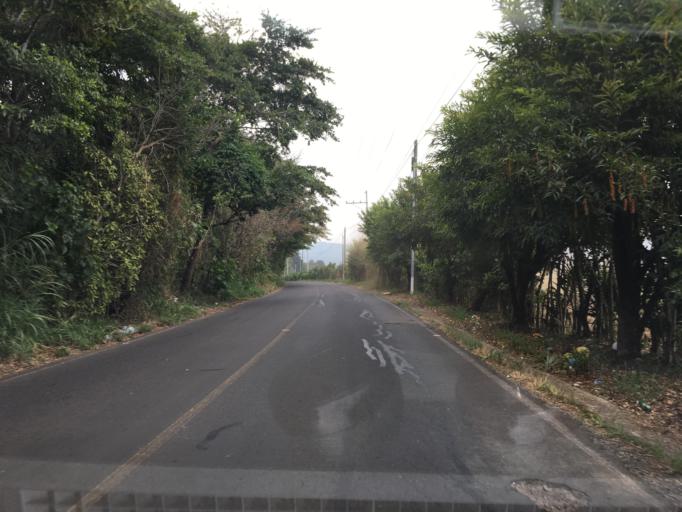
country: GT
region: Guatemala
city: Fraijanes
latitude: 14.3769
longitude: -90.4897
